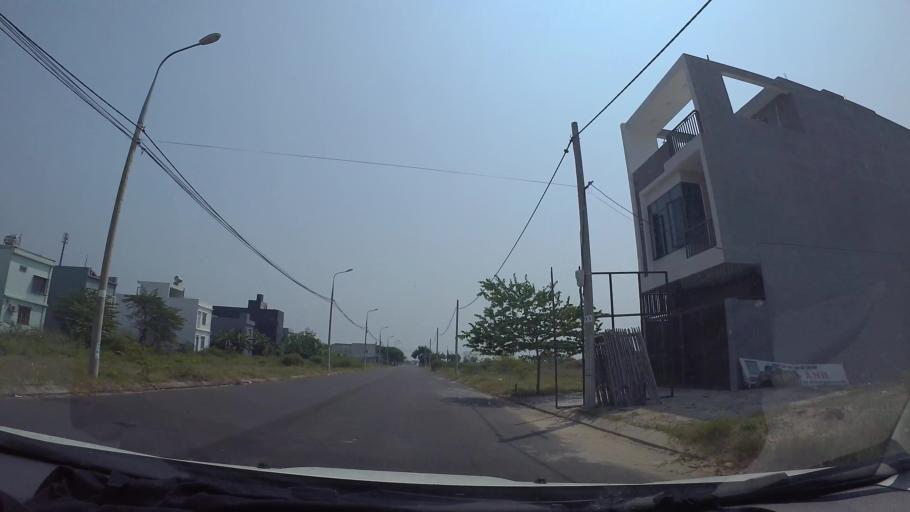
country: VN
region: Da Nang
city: Cam Le
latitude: 15.9808
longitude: 108.2115
